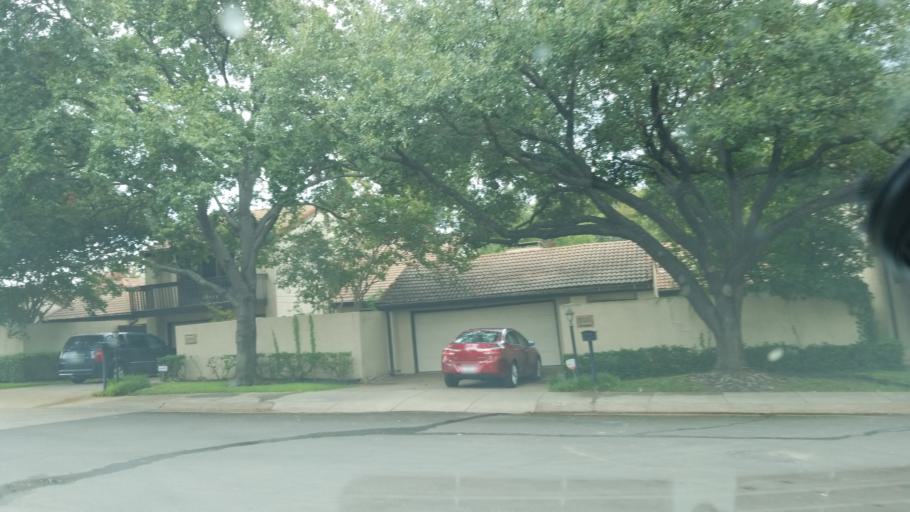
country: US
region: Texas
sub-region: Dallas County
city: Richardson
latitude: 32.8950
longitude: -96.7260
